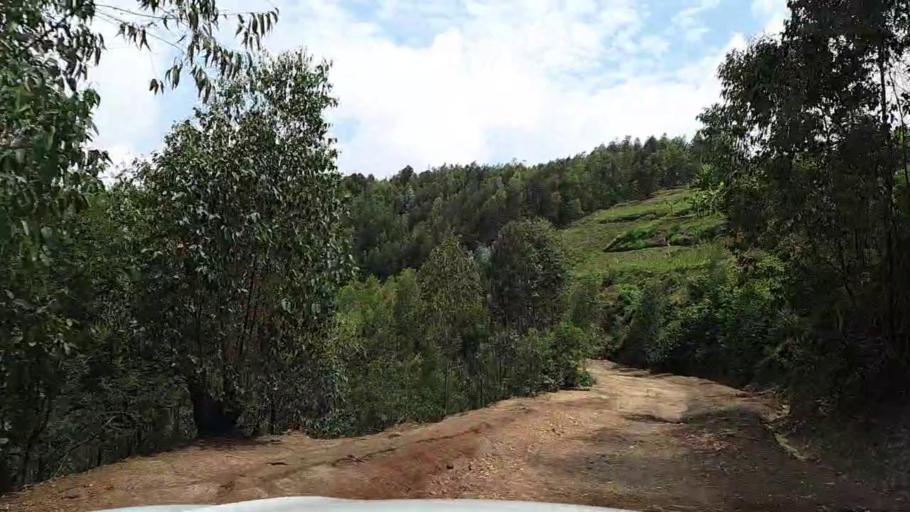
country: RW
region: Southern Province
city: Gikongoro
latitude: -2.3393
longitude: 29.5146
